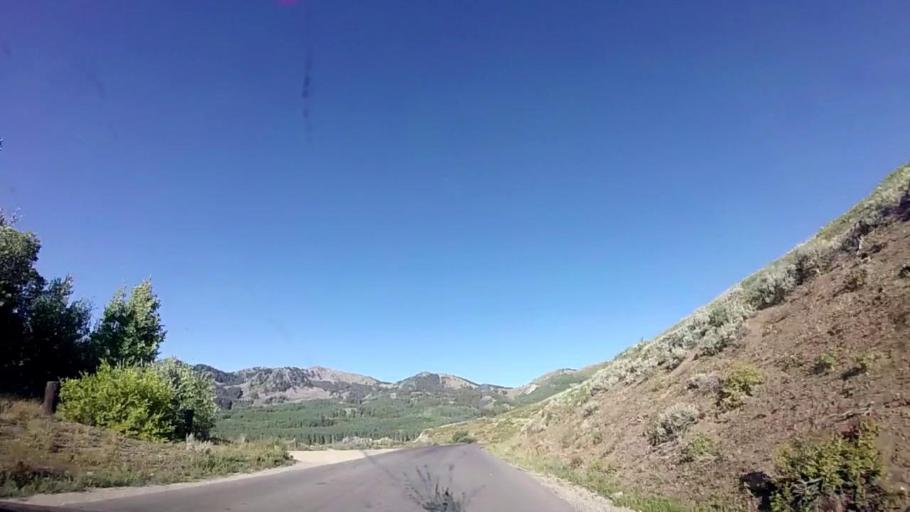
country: US
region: Utah
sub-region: Summit County
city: Park City
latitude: 40.6047
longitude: -111.5188
